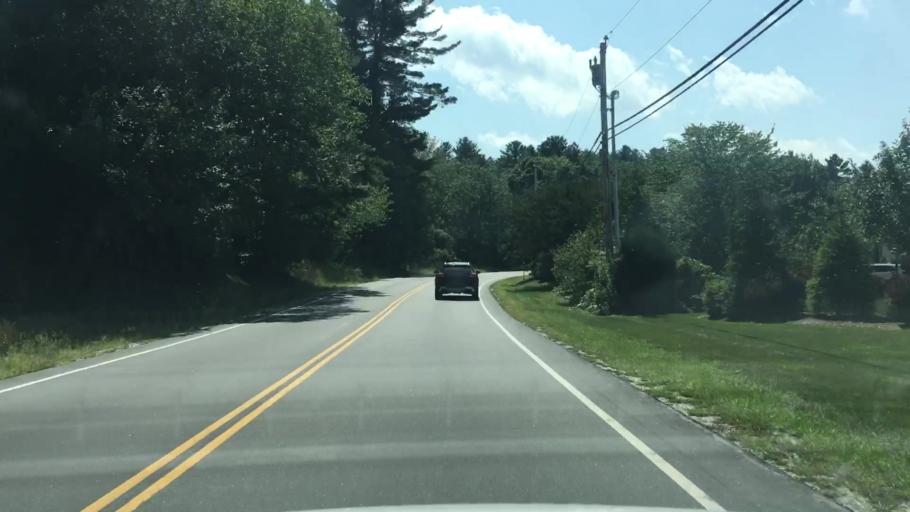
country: US
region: New Hampshire
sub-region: Rockingham County
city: Windham
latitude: 42.7989
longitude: -71.3524
